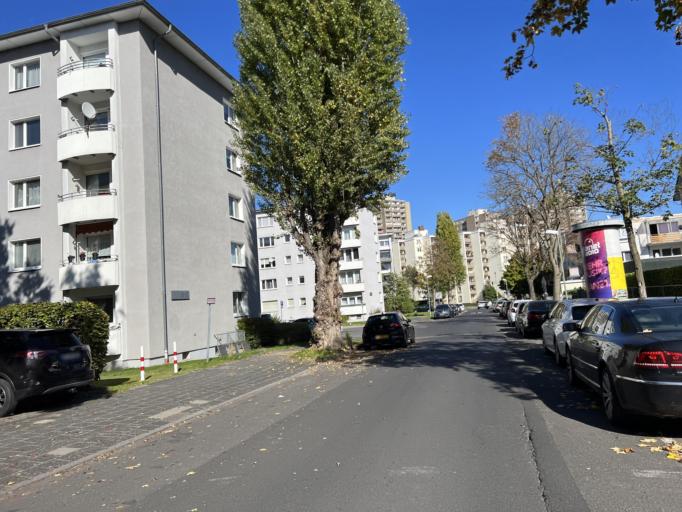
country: DE
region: Hesse
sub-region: Regierungsbezirk Darmstadt
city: Offenbach
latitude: 50.0822
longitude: 8.7738
